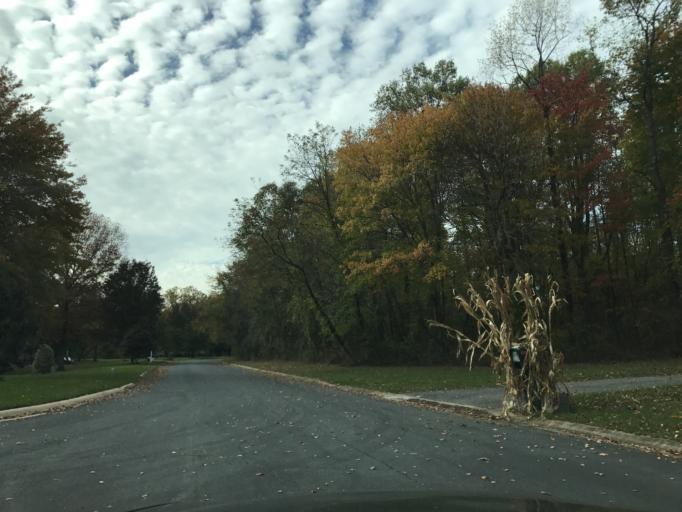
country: US
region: Maryland
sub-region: Harford County
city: Pleasant Hills
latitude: 39.4818
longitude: -76.3762
